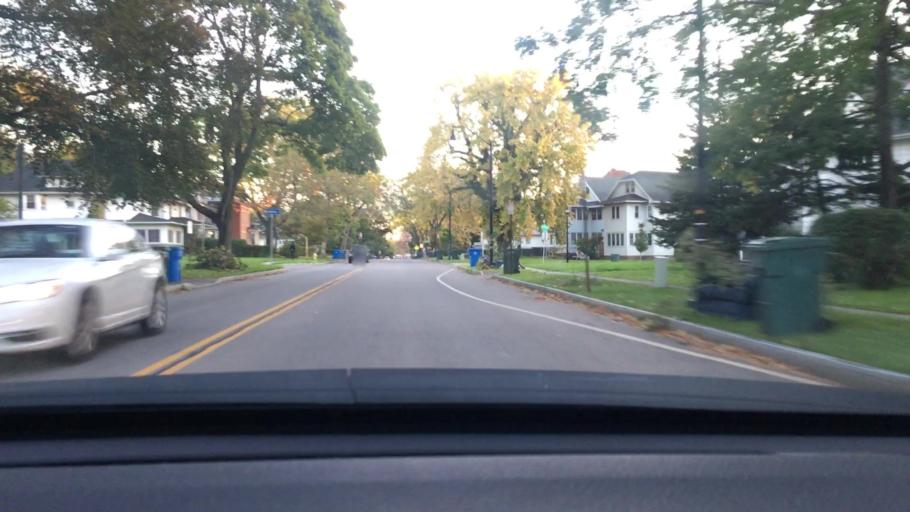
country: US
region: New York
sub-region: Monroe County
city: Brighton
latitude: 43.1725
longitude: -77.5594
